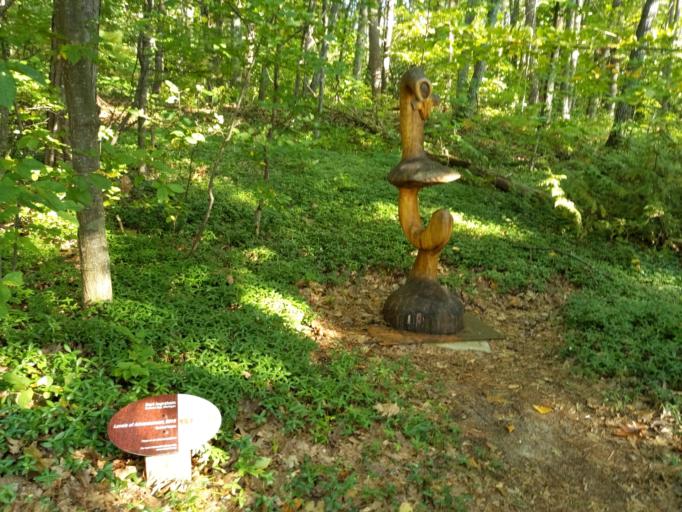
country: US
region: Michigan
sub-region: Antrim County
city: Elk Rapids
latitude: 44.8869
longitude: -85.4233
